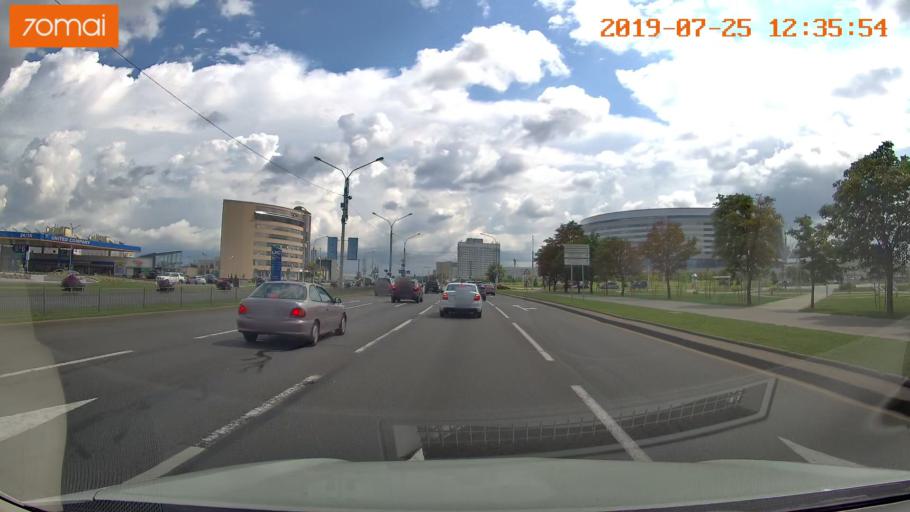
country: BY
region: Minsk
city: Zhdanovichy
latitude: 53.9379
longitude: 27.4775
